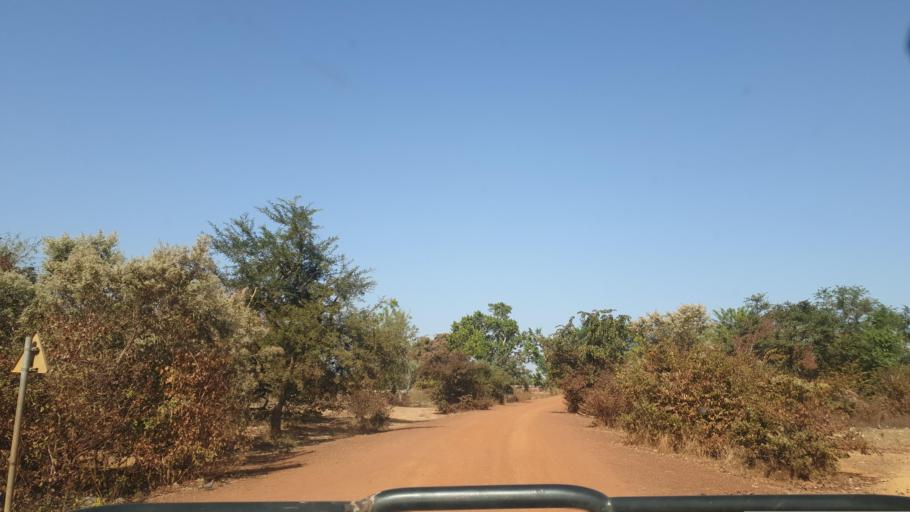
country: ML
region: Sikasso
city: Bougouni
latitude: 11.8110
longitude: -6.9333
